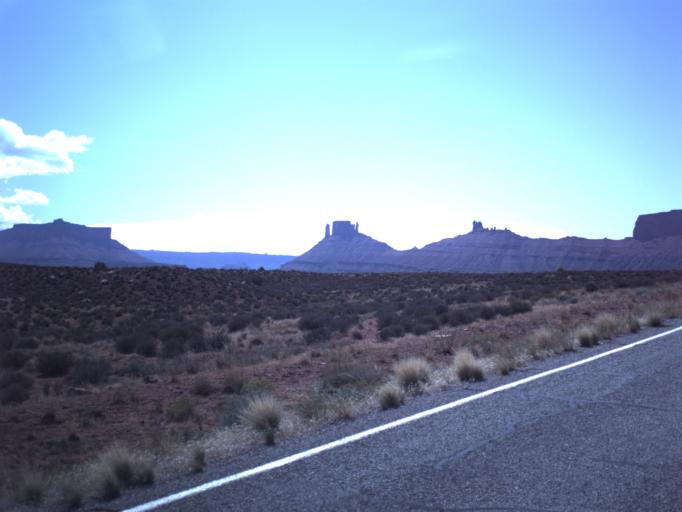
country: US
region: Utah
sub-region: Grand County
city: Moab
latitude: 38.7256
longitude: -109.3532
